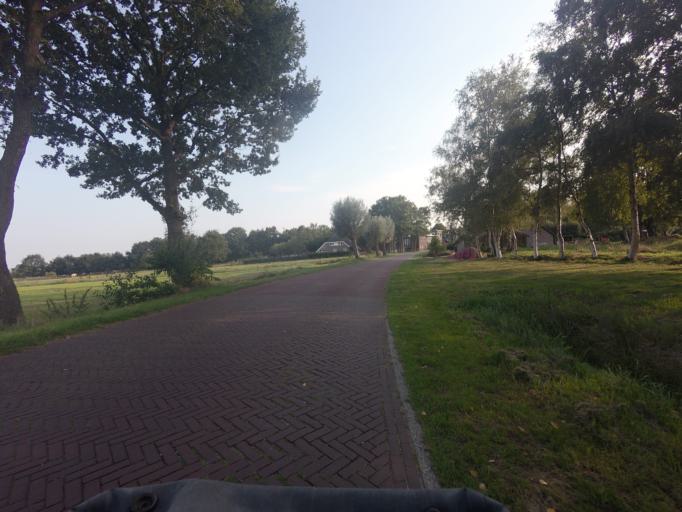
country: NL
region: Drenthe
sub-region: Gemeente Tynaarlo
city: Vries
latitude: 53.1191
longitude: 6.5342
